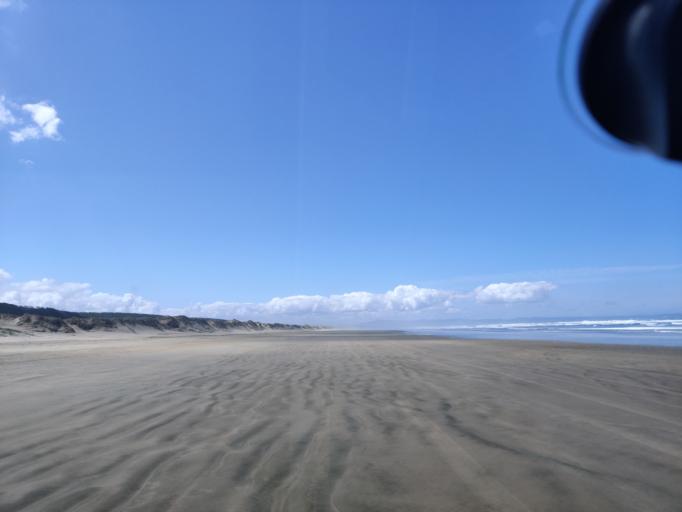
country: NZ
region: Northland
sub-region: Far North District
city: Kaitaia
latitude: -34.9496
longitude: 173.1214
